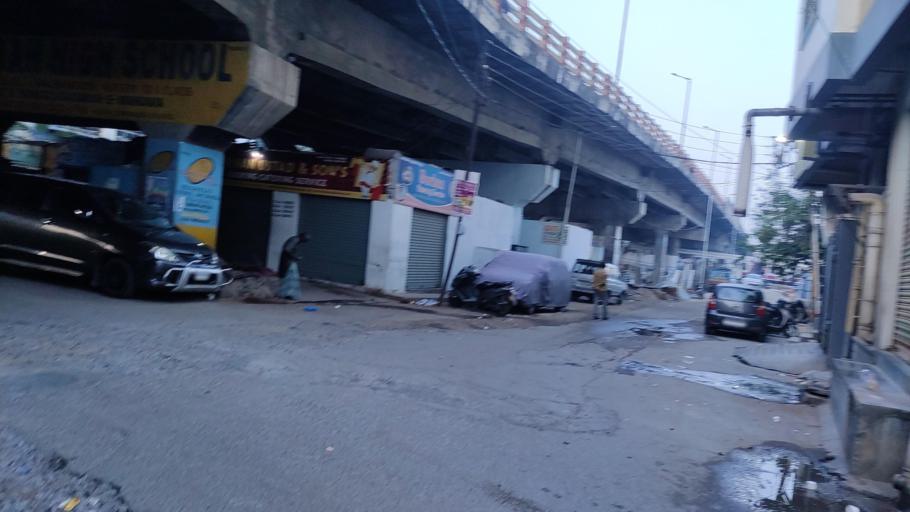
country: IN
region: Telangana
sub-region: Rangareddi
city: Gaddi Annaram
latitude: 17.3671
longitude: 78.4910
